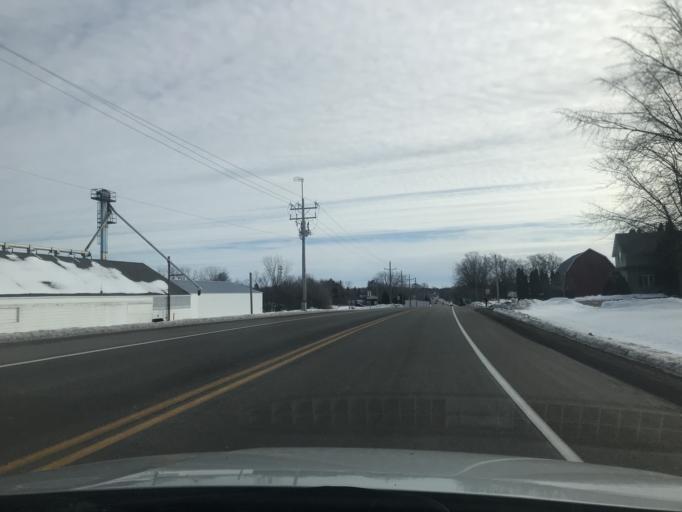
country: US
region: Wisconsin
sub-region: Oconto County
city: Oconto Falls
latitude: 44.8843
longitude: -88.1545
